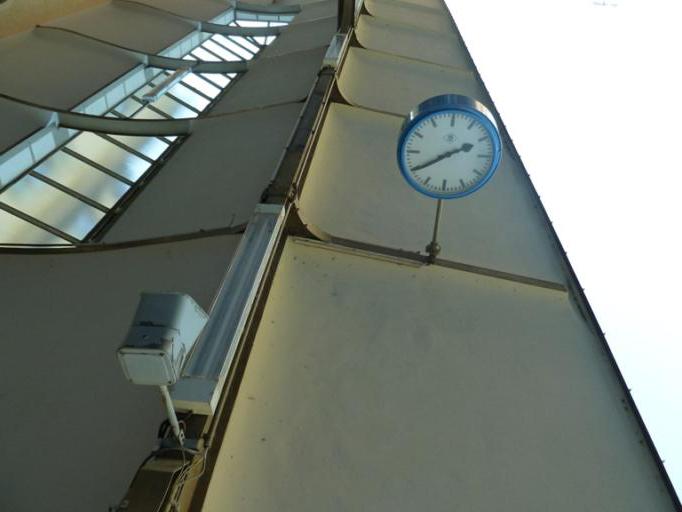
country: DE
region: Baden-Wuerttemberg
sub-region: Tuebingen Region
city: Balingen
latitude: 48.2783
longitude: 8.8504
